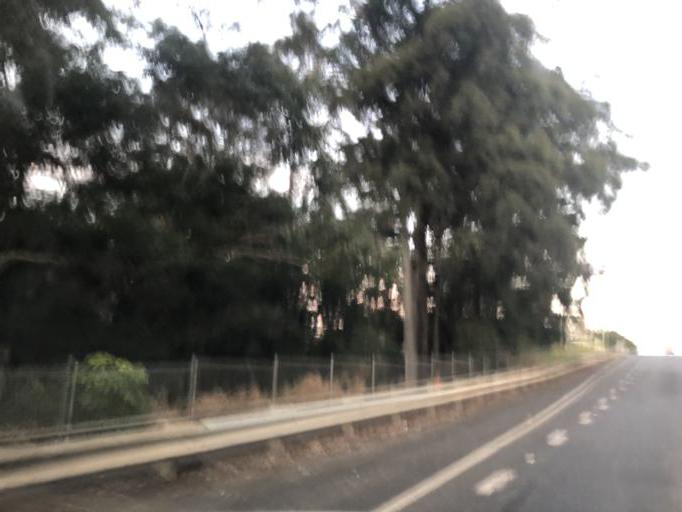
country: AU
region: New South Wales
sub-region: Coffs Harbour
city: Woolgoolga
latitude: -30.1063
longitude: 153.1887
